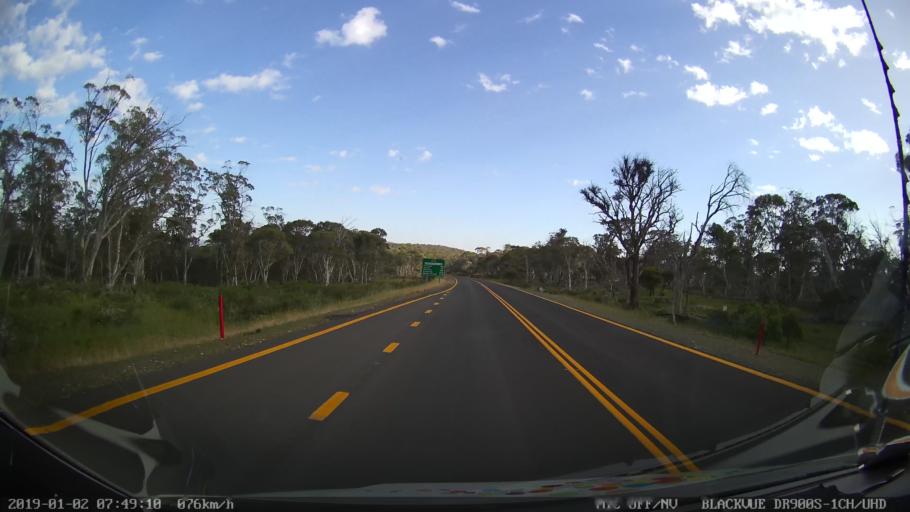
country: AU
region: New South Wales
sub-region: Tumut Shire
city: Tumut
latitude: -35.7448
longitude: 148.5216
